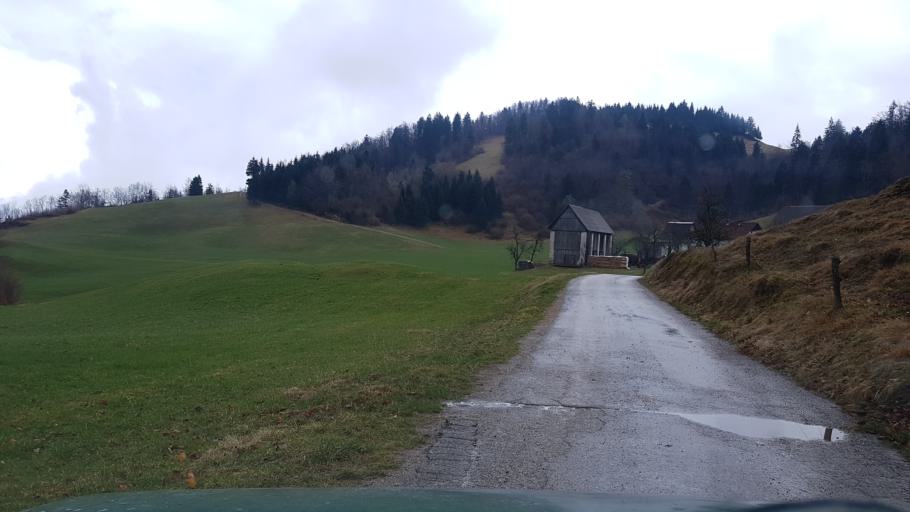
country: SI
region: Cerkno
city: Cerkno
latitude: 46.1420
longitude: 13.8872
